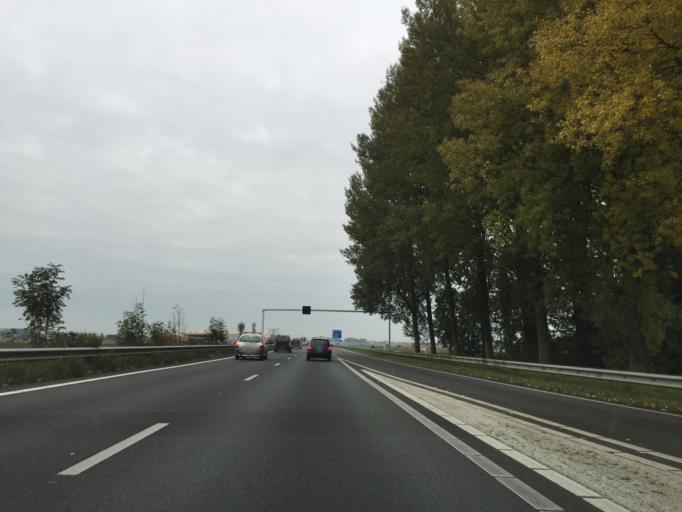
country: NL
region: North Brabant
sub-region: Gemeente Waalwijk
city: Waalwijk
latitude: 51.6942
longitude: 5.0144
